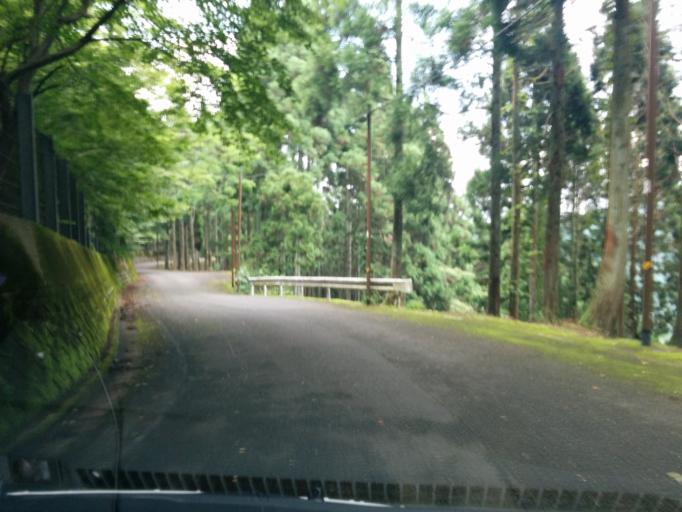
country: JP
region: Kyoto
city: Miyazu
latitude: 35.4531
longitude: 135.1125
